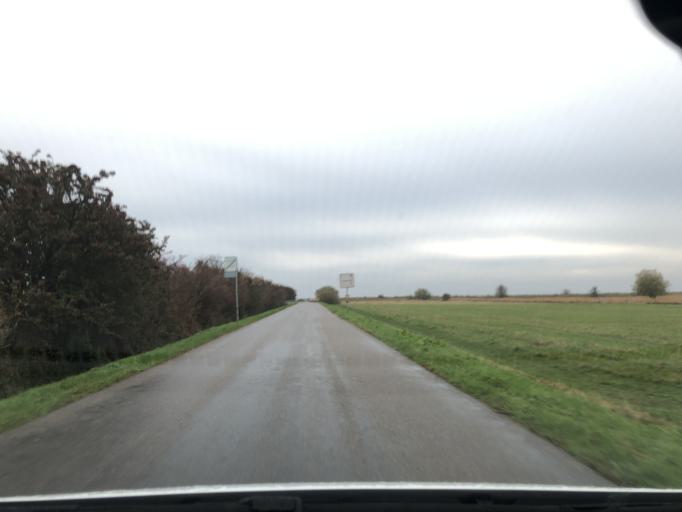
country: DK
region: Capital Region
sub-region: Dragor Kommune
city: Dragor
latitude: 55.5802
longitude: 12.6399
